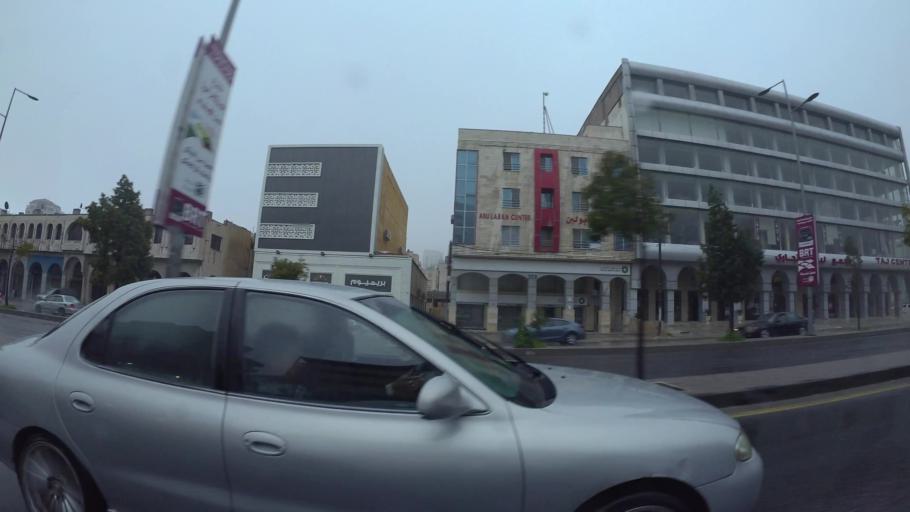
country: JO
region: Amman
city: Al Jubayhah
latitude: 32.0201
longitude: 35.8620
